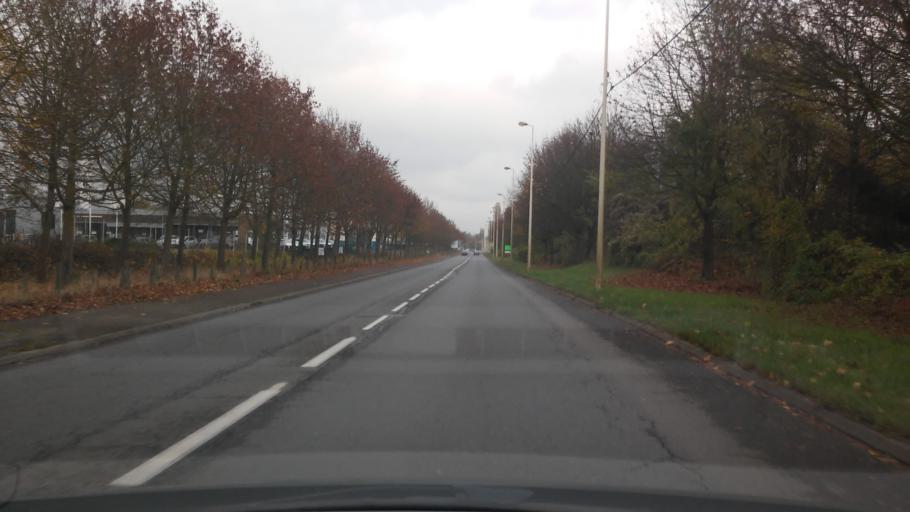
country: FR
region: Lorraine
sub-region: Departement de la Moselle
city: Terville
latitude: 49.3377
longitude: 6.1588
